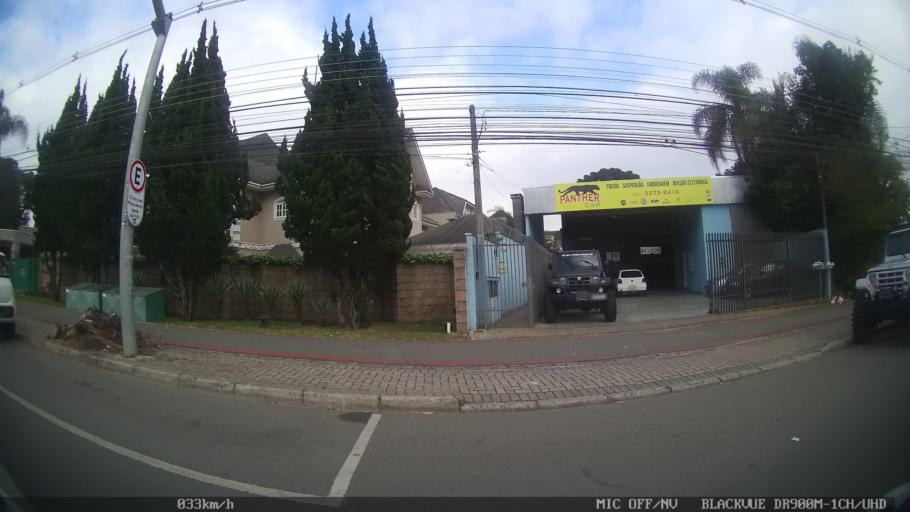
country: BR
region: Parana
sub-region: Curitiba
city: Curitiba
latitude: -25.3980
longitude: -49.3346
